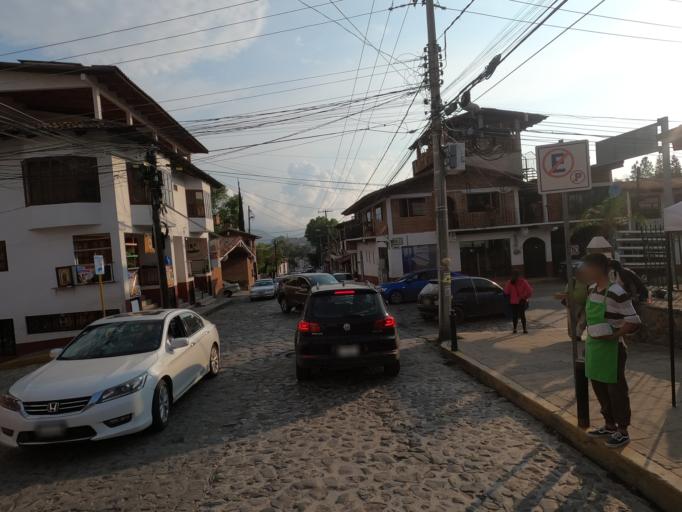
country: MX
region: Mexico
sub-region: Valle de Bravo
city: Colonia Rincon Villa del Valle
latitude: 19.2027
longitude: -100.1259
